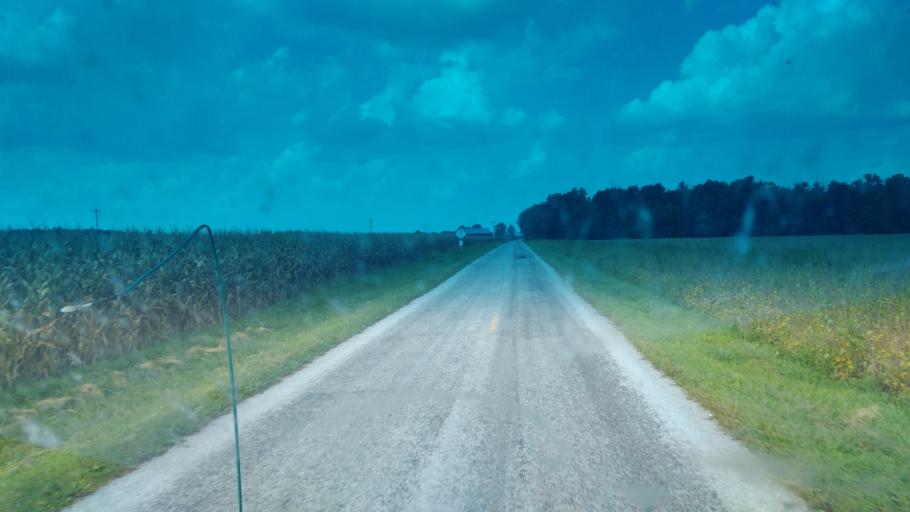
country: US
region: Ohio
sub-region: Hardin County
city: Kenton
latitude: 40.7321
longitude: -83.6022
